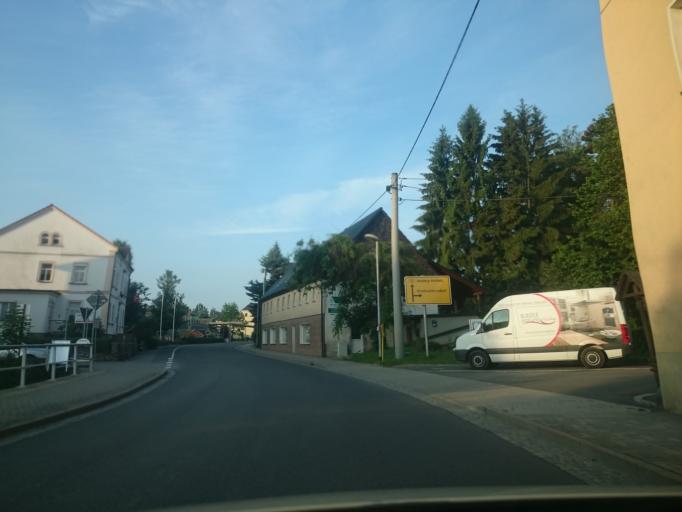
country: DE
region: Saxony
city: Grosshartmannsdorf
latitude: 50.7967
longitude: 13.3190
